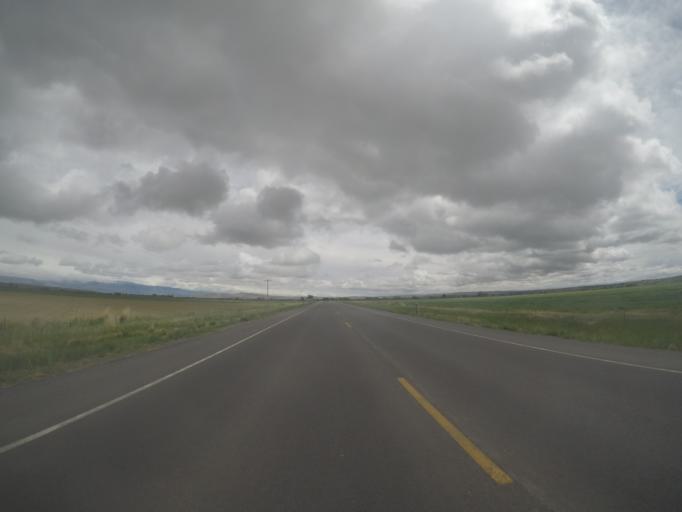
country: US
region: Wyoming
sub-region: Big Horn County
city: Lovell
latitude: 44.8677
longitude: -108.4530
